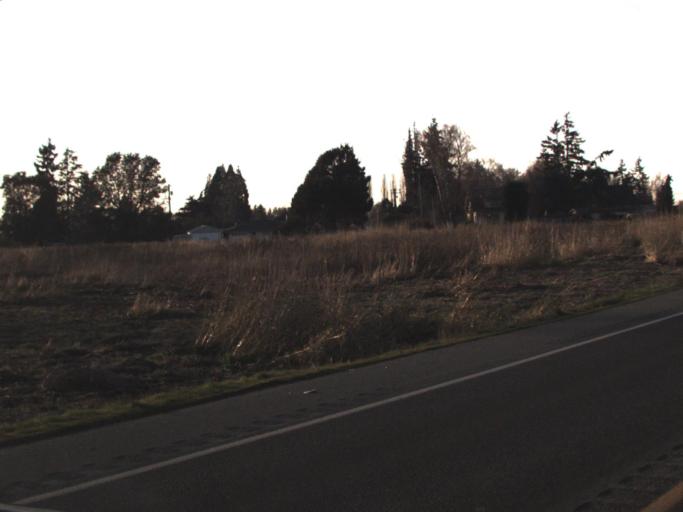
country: US
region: Washington
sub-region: Skagit County
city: Mount Vernon
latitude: 48.4353
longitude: -122.3765
